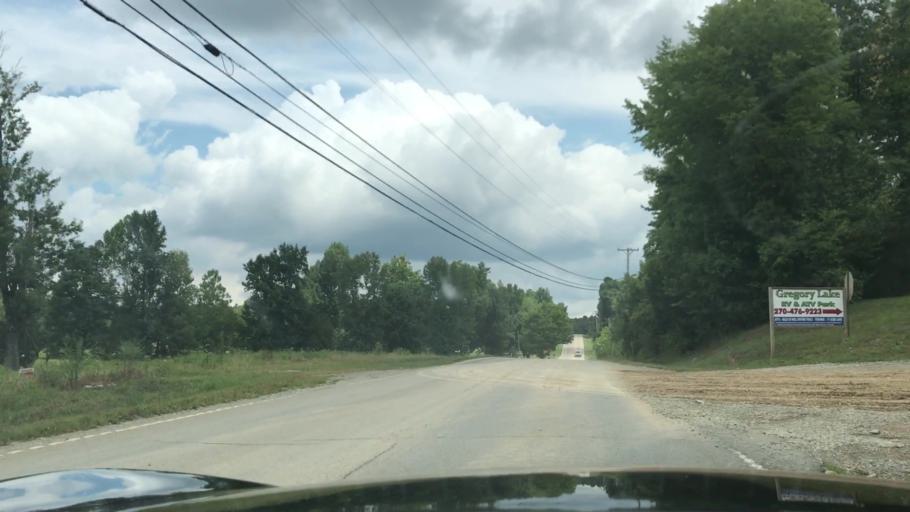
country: US
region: Kentucky
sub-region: Muhlenberg County
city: Central City
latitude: 37.2094
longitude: -87.0692
